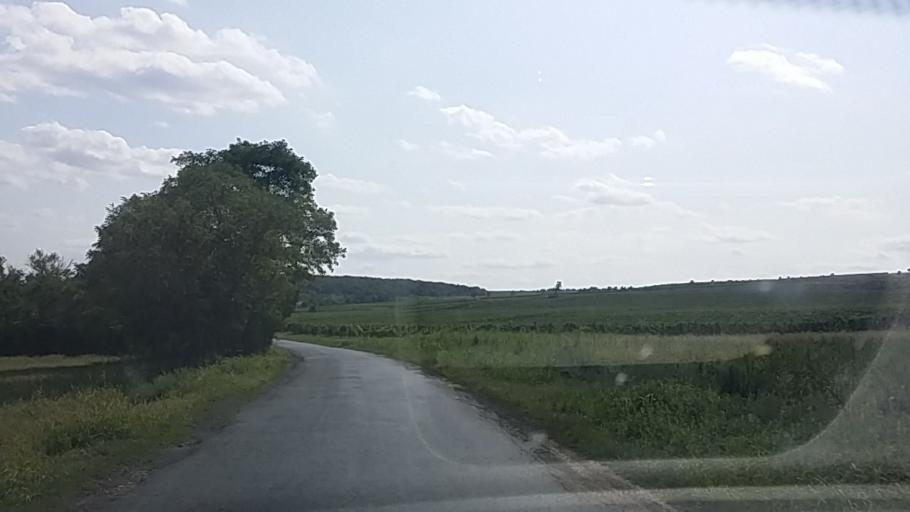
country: HU
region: Gyor-Moson-Sopron
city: Fertorakos
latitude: 47.6863
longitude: 16.6645
